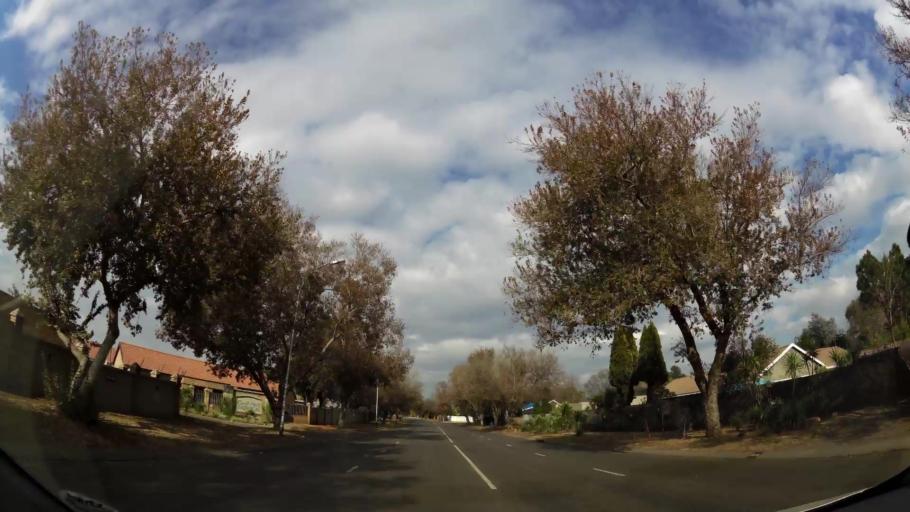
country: ZA
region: Gauteng
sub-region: Sedibeng District Municipality
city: Meyerton
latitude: -26.5508
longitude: 28.0334
